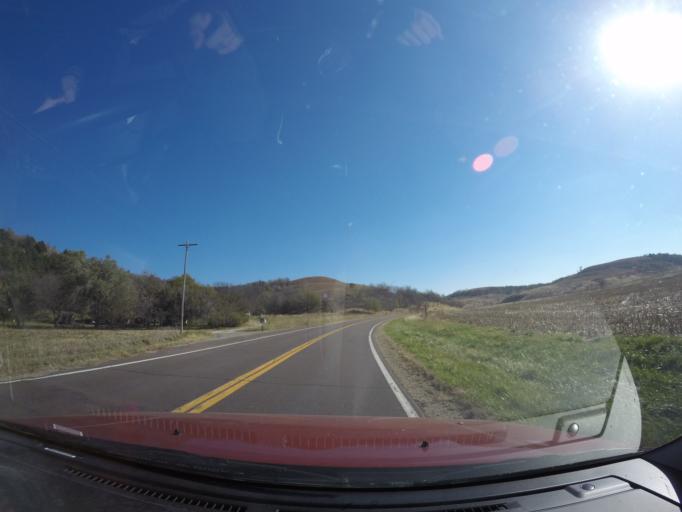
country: US
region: Kansas
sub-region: Geary County
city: Grandview Plaza
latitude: 39.0079
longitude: -96.7328
